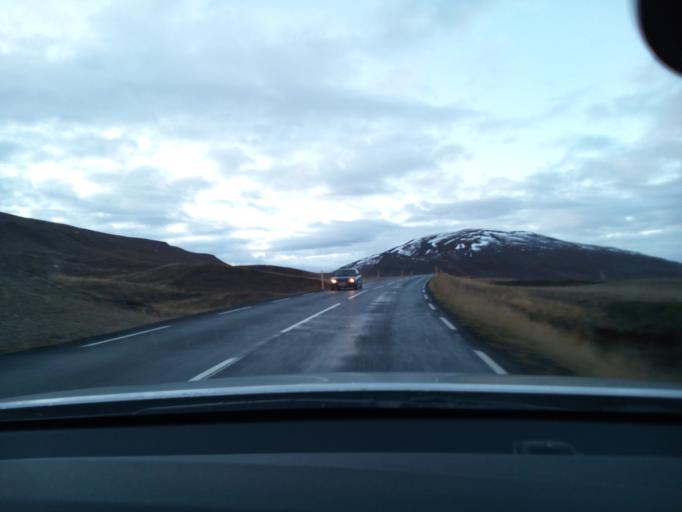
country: IS
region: Northeast
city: Akureyri
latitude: 65.7897
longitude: -17.9298
